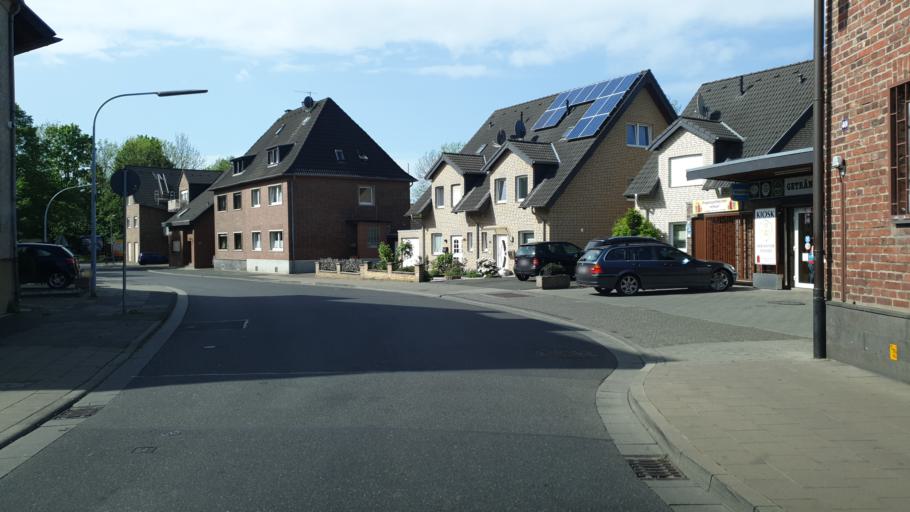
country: DE
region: North Rhine-Westphalia
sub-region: Regierungsbezirk Koln
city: Bergheim
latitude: 50.9409
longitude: 6.6772
